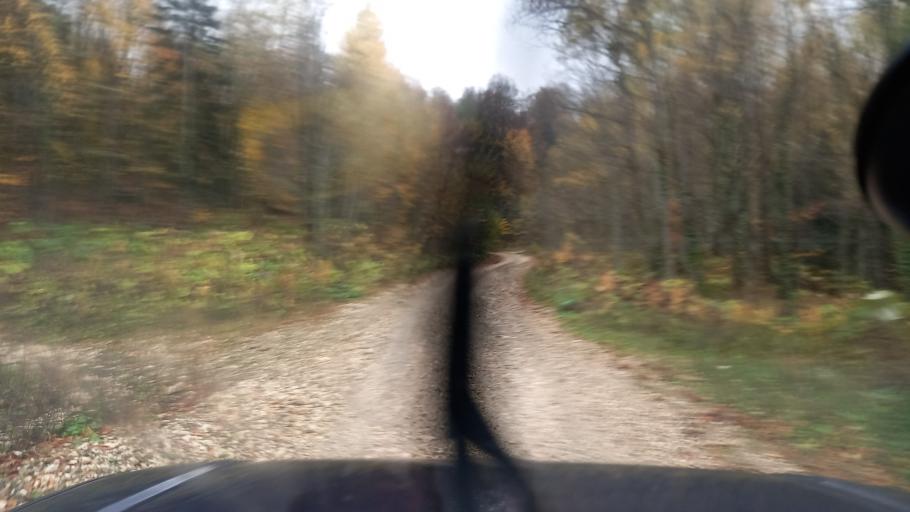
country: RU
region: Krasnodarskiy
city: Neftegorsk
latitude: 44.0273
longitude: 39.8412
